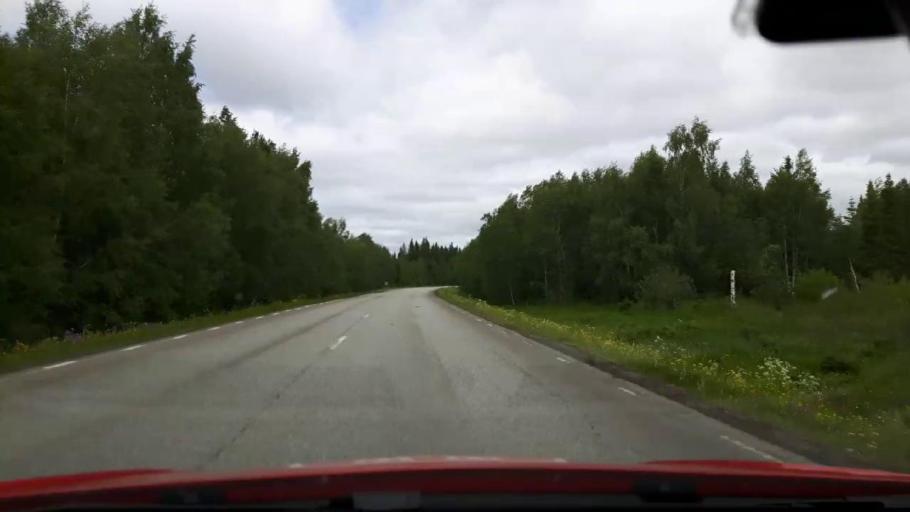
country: SE
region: Jaemtland
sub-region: Krokoms Kommun
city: Krokom
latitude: 63.3757
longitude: 14.5060
